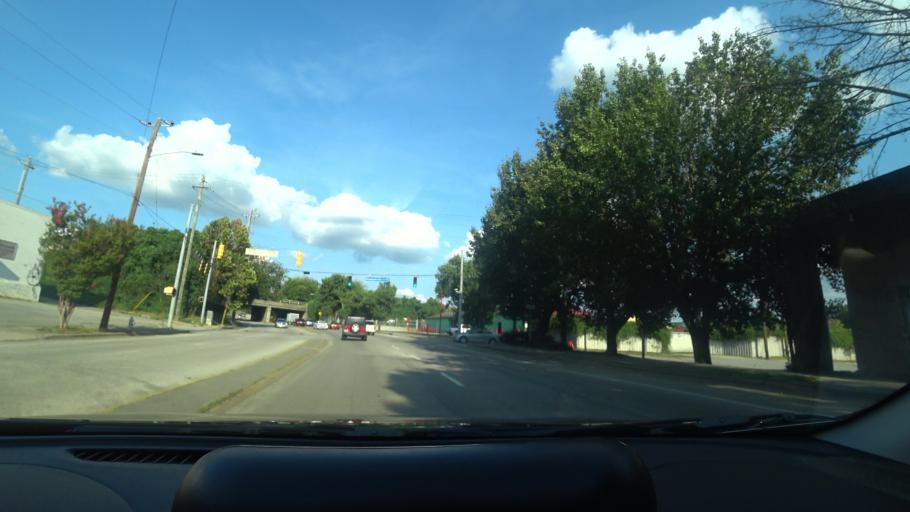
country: US
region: Georgia
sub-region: Fulton County
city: Atlanta
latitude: 33.7366
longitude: -84.4052
